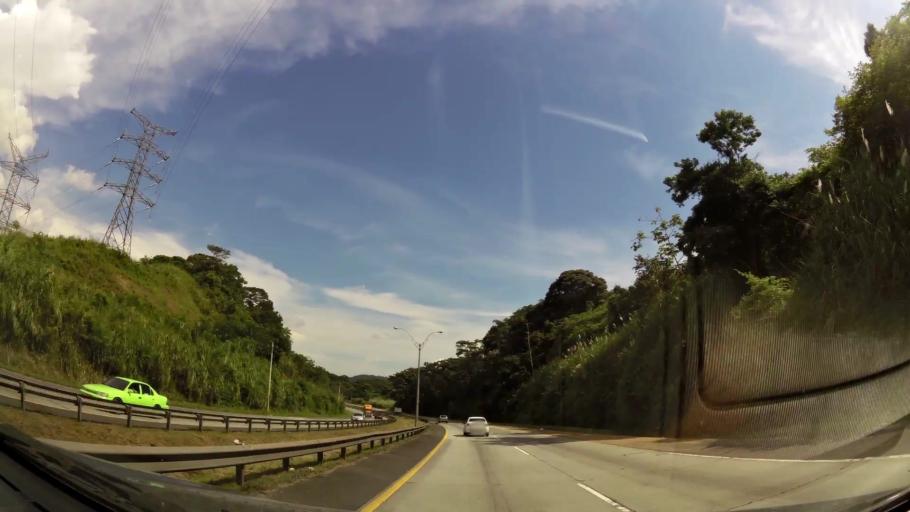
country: PA
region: Panama
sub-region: Distrito de Panama
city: Paraiso
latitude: 9.0284
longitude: -79.6132
